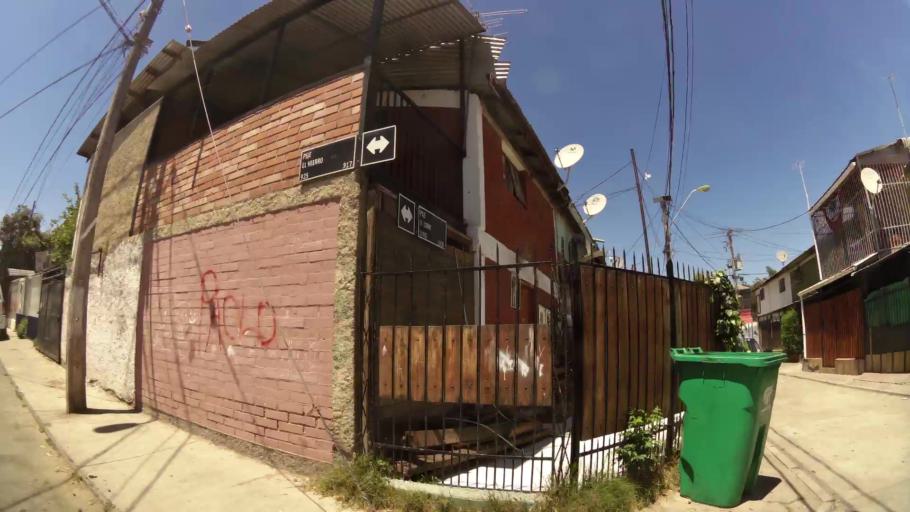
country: CL
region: Santiago Metropolitan
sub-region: Provincia de Santiago
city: La Pintana
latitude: -33.5765
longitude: -70.6660
